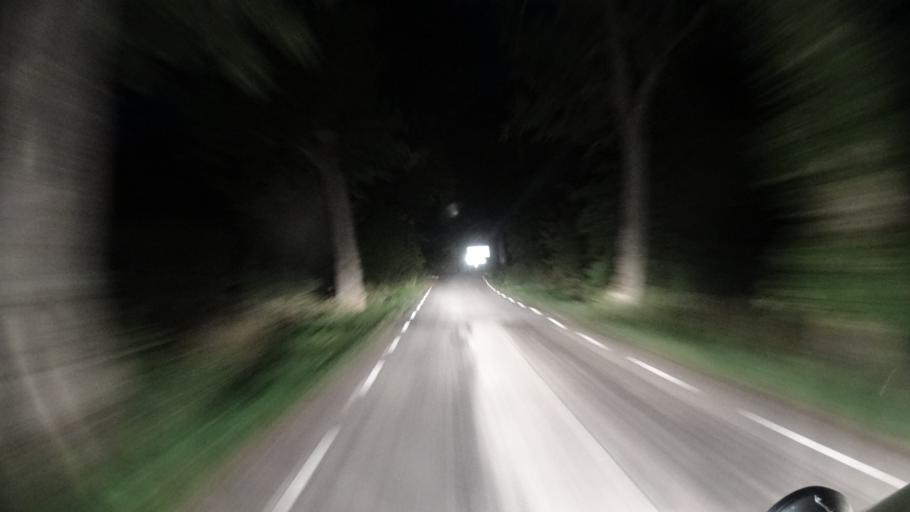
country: SE
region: OEstergoetland
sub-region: Vadstena Kommun
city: Herrestad
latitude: 58.3209
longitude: 14.8417
